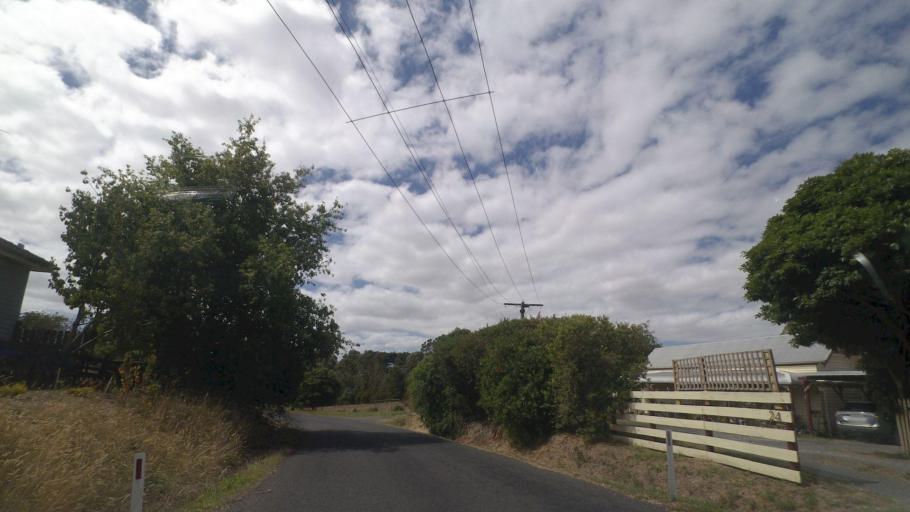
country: AU
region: Victoria
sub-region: Bass Coast
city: North Wonthaggi
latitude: -38.4099
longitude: 145.7631
